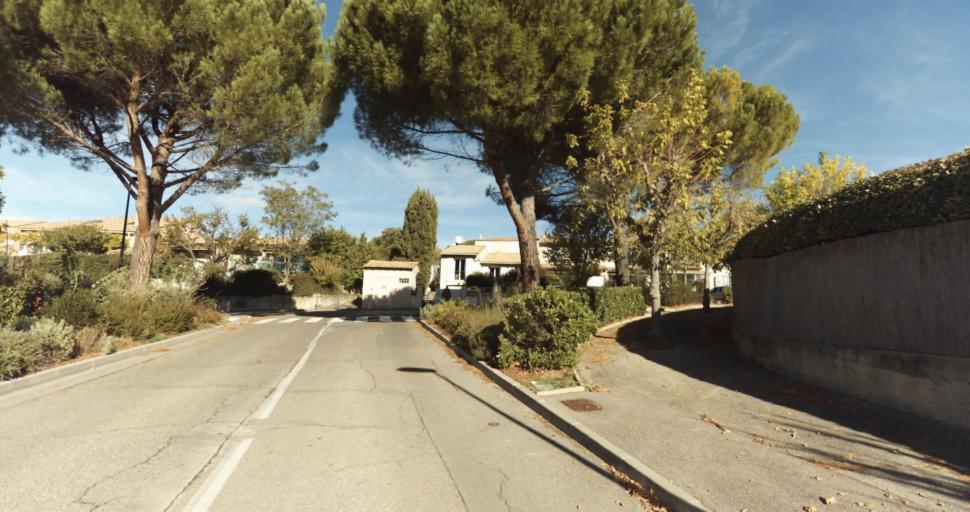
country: FR
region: Provence-Alpes-Cote d'Azur
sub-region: Departement des Bouches-du-Rhone
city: Venelles
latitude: 43.5957
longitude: 5.4788
